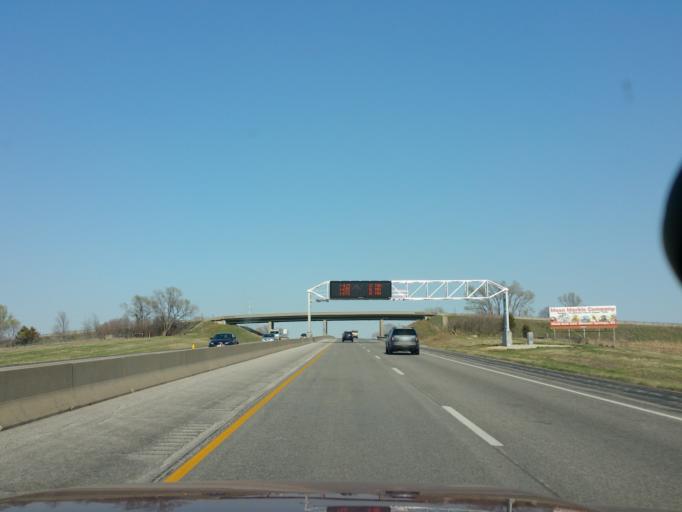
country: US
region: Kansas
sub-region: Leavenworth County
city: Basehor
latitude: 39.0751
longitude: -94.9850
